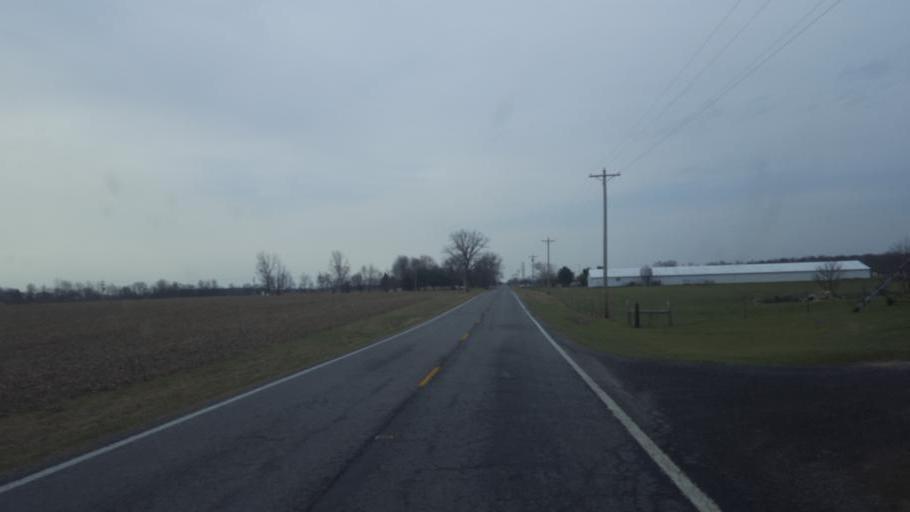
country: US
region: Ohio
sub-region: Morrow County
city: Cardington
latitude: 40.6045
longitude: -82.9624
